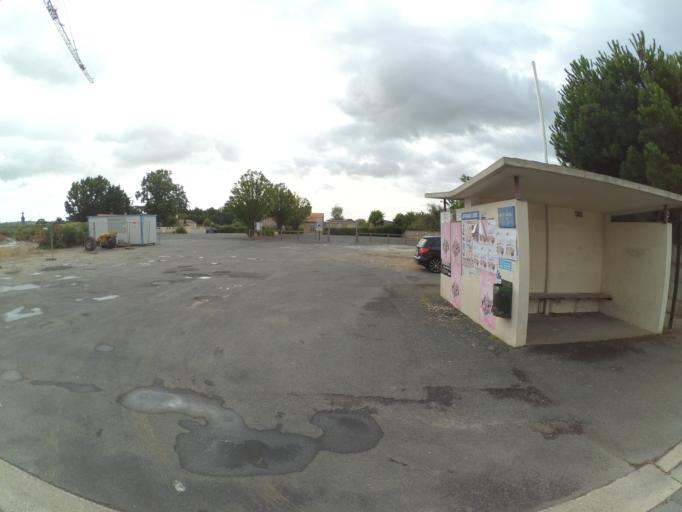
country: FR
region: Pays de la Loire
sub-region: Departement de la Vendee
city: Cugand
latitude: 47.0655
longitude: -1.2544
